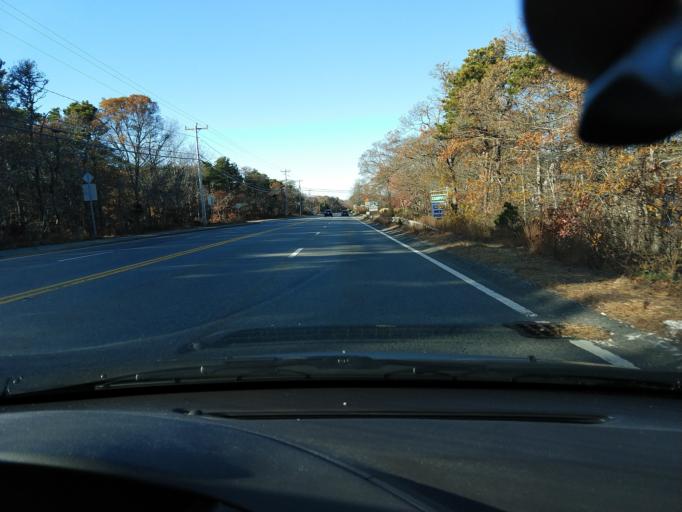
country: US
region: Massachusetts
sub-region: Barnstable County
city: Eastham
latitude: 41.8445
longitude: -69.9839
